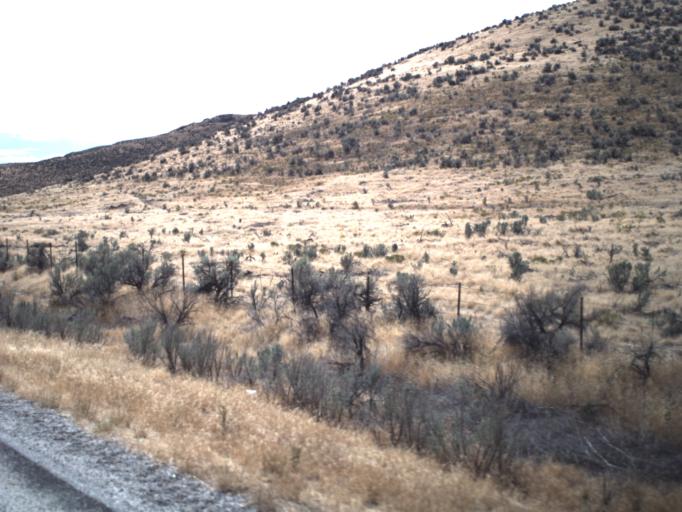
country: US
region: Utah
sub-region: Box Elder County
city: Tremonton
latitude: 41.7058
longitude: -112.4499
